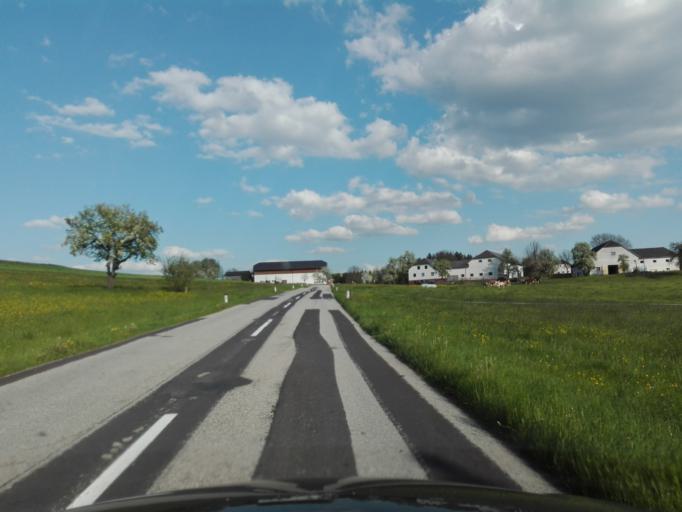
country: AT
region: Upper Austria
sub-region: Politischer Bezirk Rohrbach
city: Atzesberg
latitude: 48.4751
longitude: 13.9456
